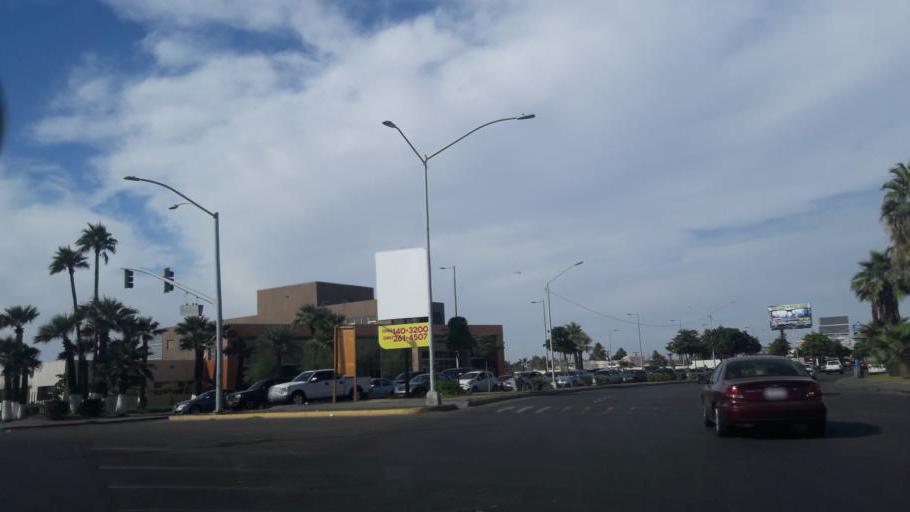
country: MX
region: Baja California
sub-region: Mexicali
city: Mexicali
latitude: 32.6250
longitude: -115.4436
